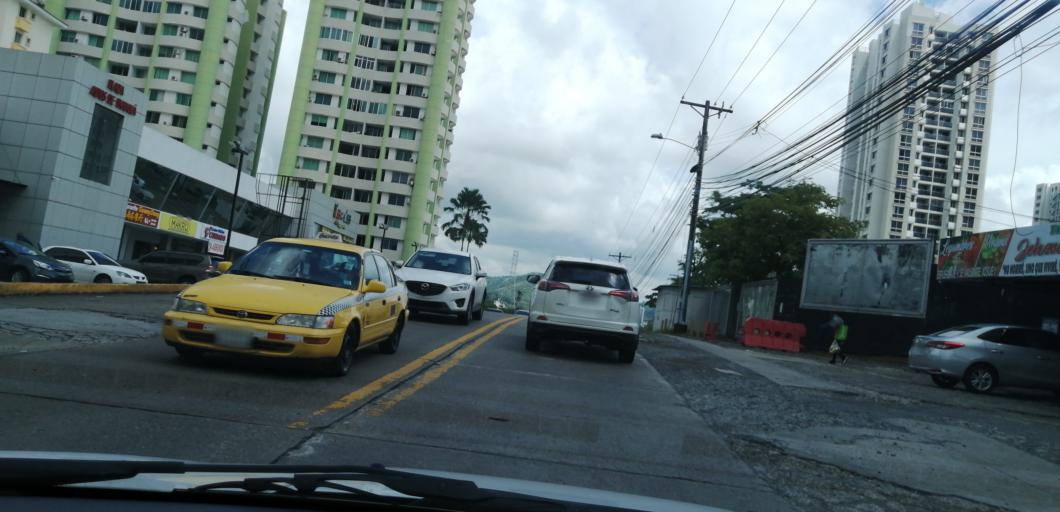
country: PA
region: Panama
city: Panama
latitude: 9.0272
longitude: -79.5242
